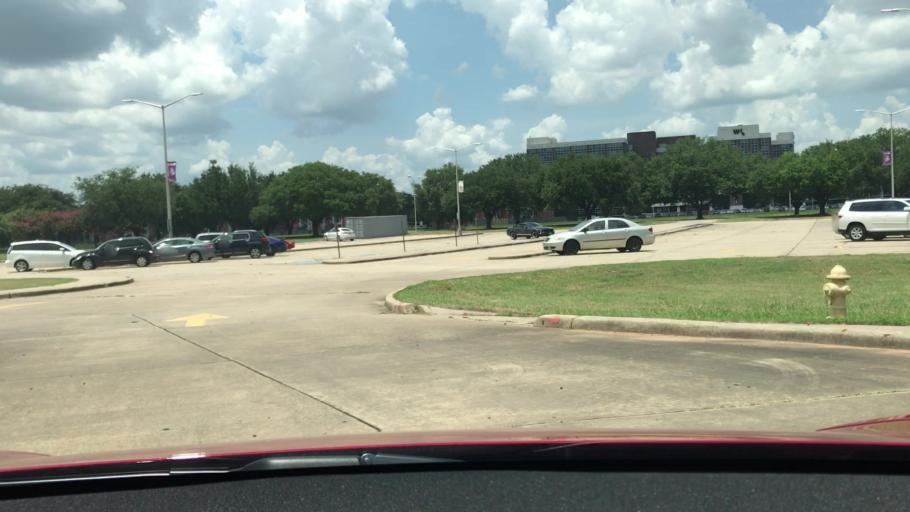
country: US
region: Louisiana
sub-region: Bossier Parish
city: Bossier City
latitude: 32.4285
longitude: -93.7065
